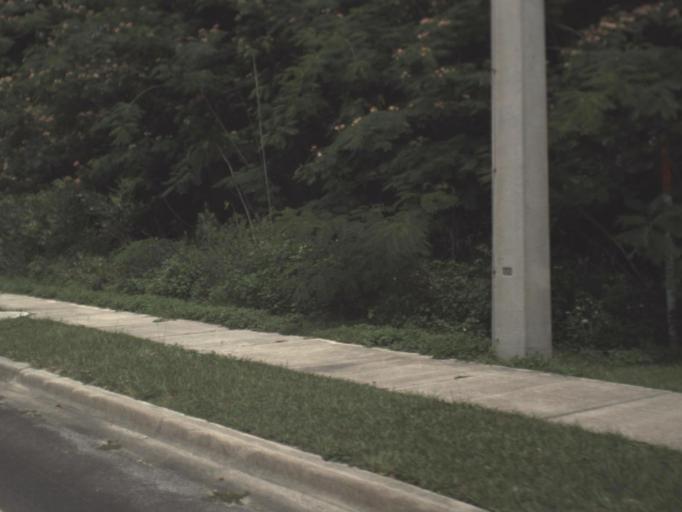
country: US
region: Florida
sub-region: Alachua County
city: Newberry
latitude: 29.6542
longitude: -82.5206
